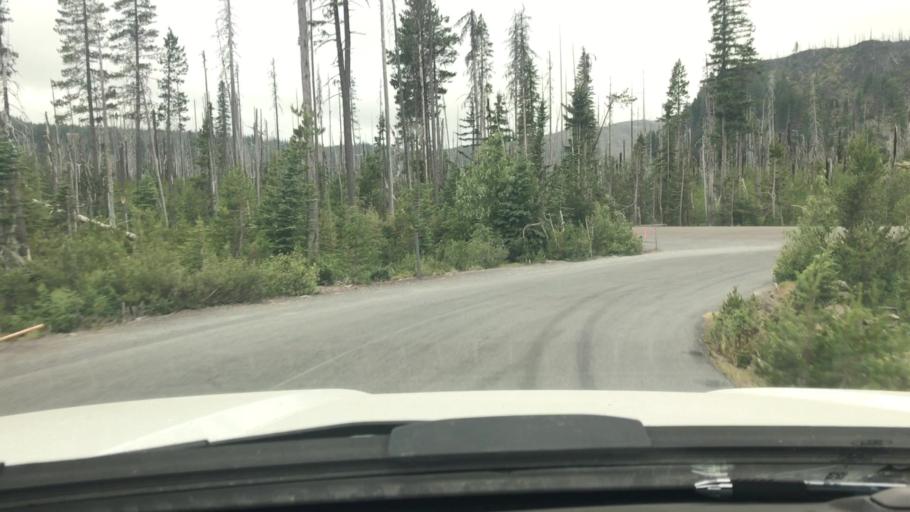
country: US
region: Oregon
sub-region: Deschutes County
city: Sisters
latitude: 44.4196
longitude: -121.8611
